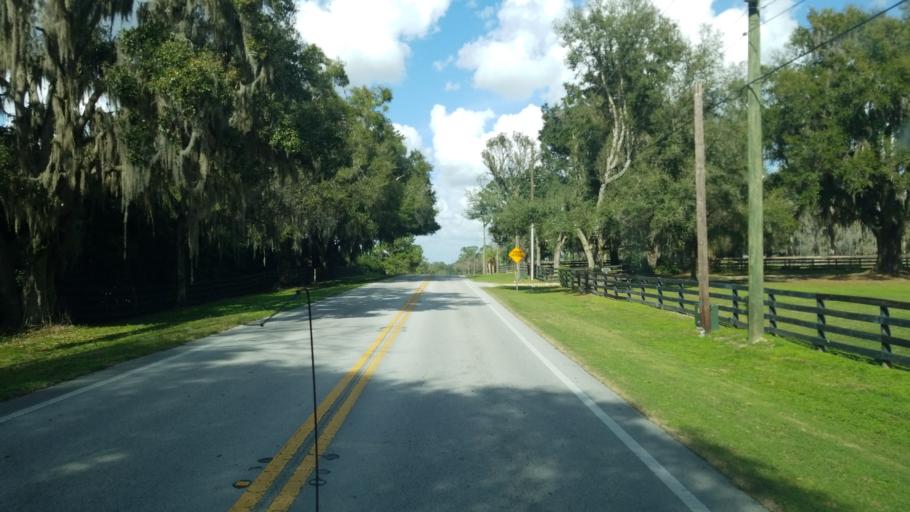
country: US
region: Florida
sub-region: Marion County
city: Ocala
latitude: 29.1065
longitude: -82.1691
